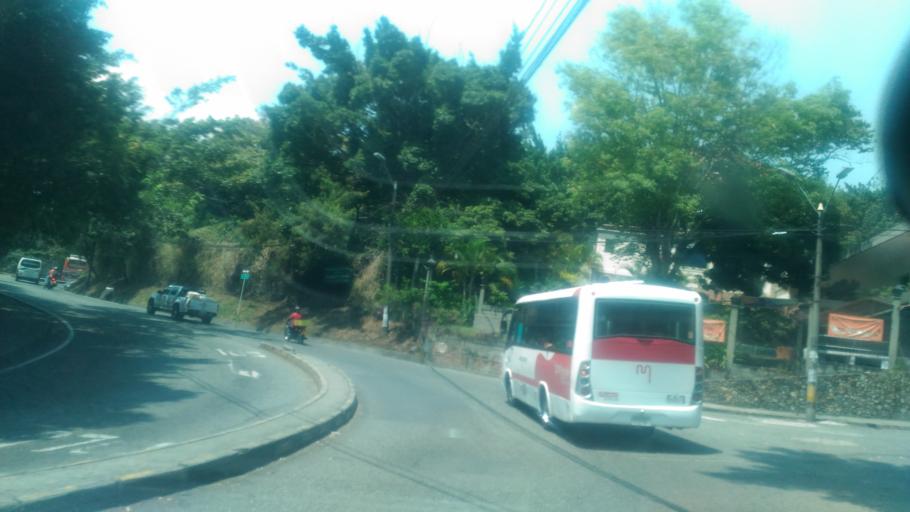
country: CO
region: Antioquia
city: Medellin
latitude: 6.2776
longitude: -75.5896
